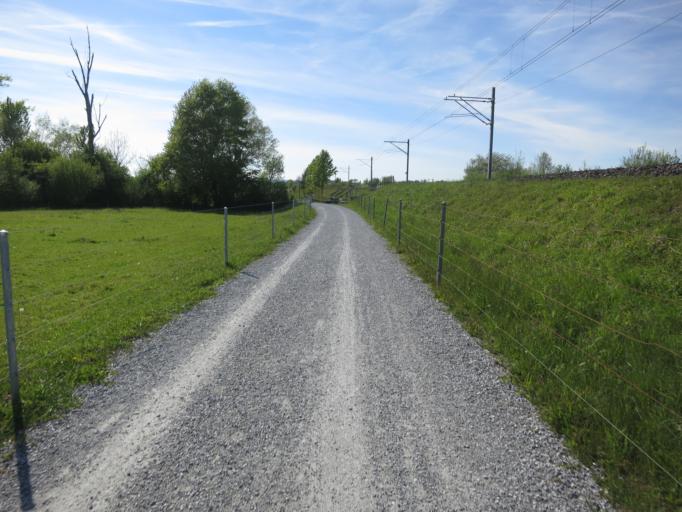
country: CH
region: Saint Gallen
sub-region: Wahlkreis See-Gaster
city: Jona
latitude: 47.2220
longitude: 8.8618
